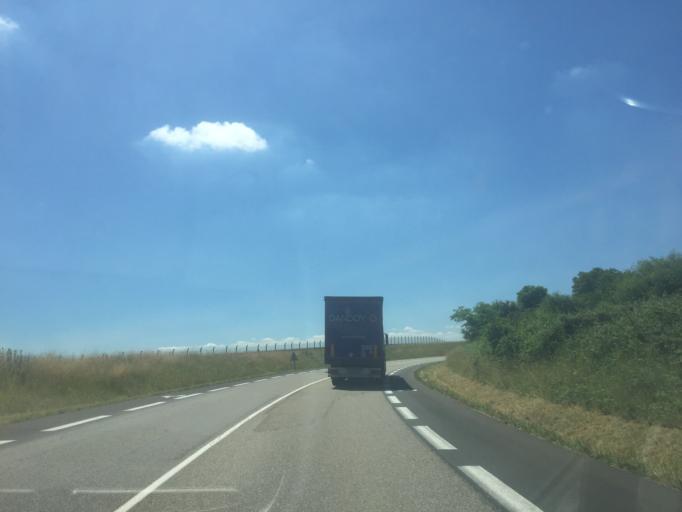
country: FR
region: Rhone-Alpes
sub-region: Departement du Rhone
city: Pusignan
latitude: 45.7453
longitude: 5.0814
